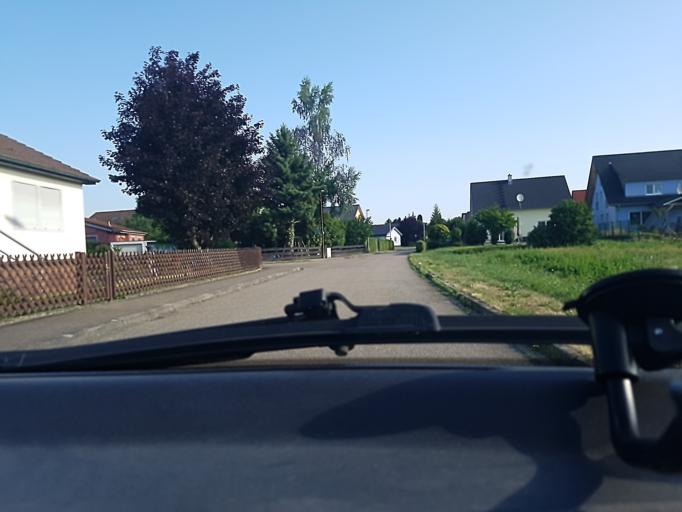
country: DE
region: Baden-Wuerttemberg
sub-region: Freiburg Region
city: Willstatt
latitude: 48.5576
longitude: 7.8815
